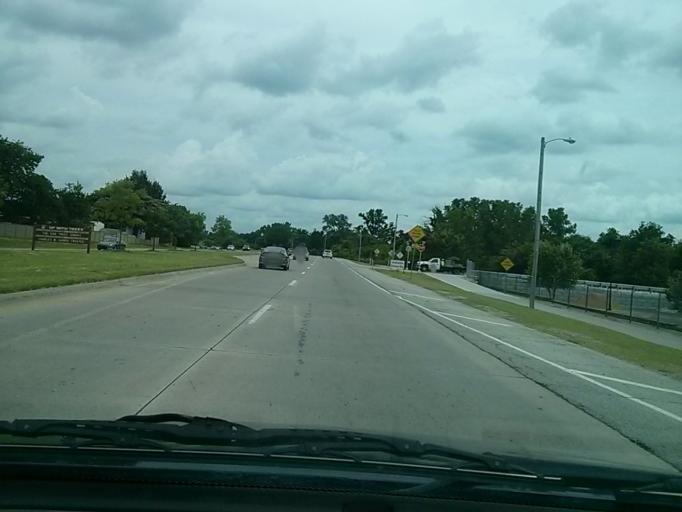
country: US
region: Oklahoma
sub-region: Tulsa County
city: Jenks
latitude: 36.0376
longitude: -95.9585
